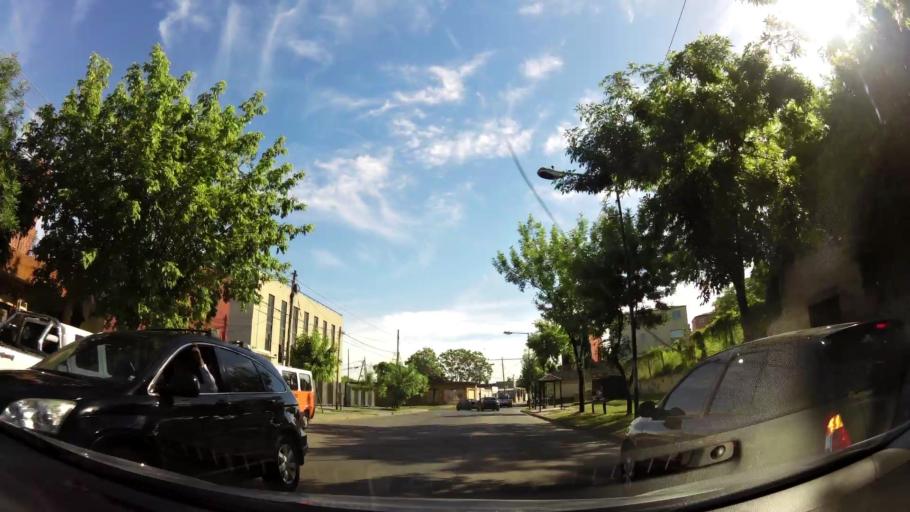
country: AR
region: Buenos Aires
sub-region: Partido de Tigre
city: Tigre
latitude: -34.4815
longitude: -58.5808
